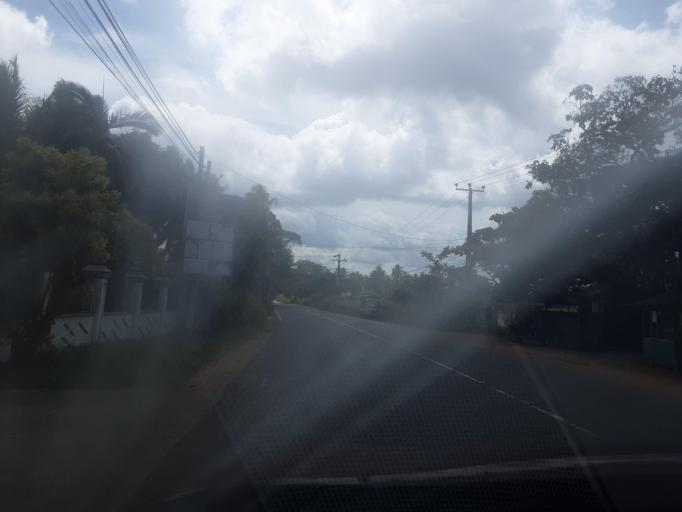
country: LK
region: North Western
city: Kuliyapitiya
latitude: 7.4772
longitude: 80.0048
